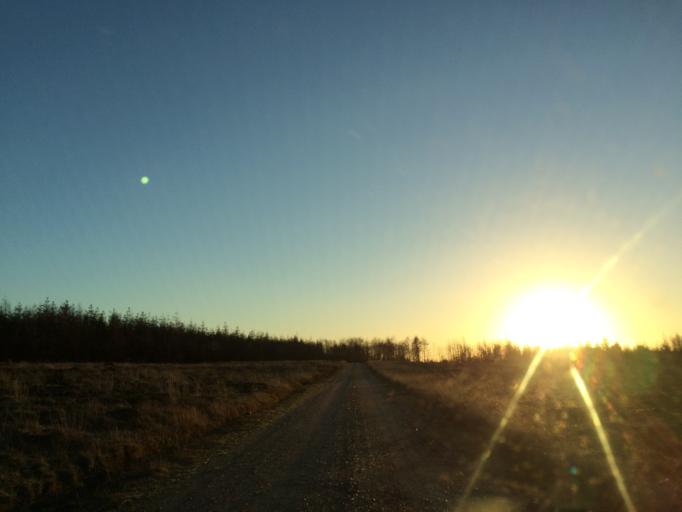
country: DK
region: Central Jutland
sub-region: Ringkobing-Skjern Kommune
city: Videbaek
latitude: 56.2183
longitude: 8.5177
